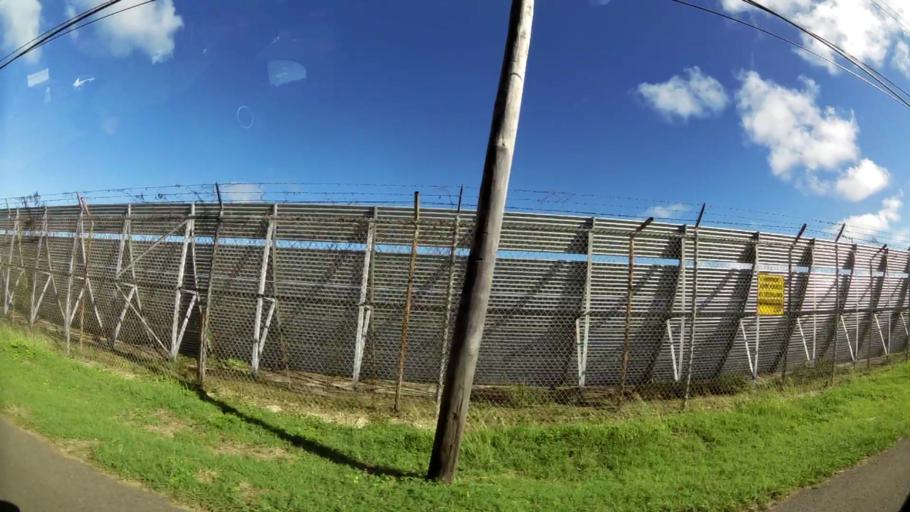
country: TT
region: Tobago
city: Scarborough
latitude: 11.1497
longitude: -60.8440
